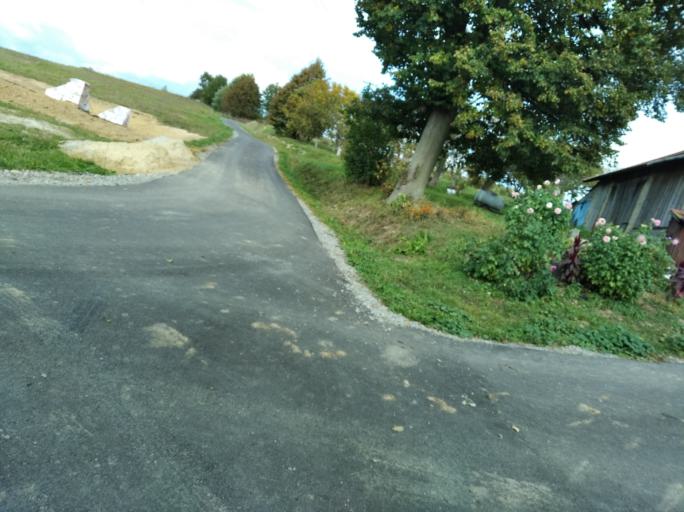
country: PL
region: Subcarpathian Voivodeship
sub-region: Powiat strzyzowski
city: Jawornik
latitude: 49.8324
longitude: 21.9005
